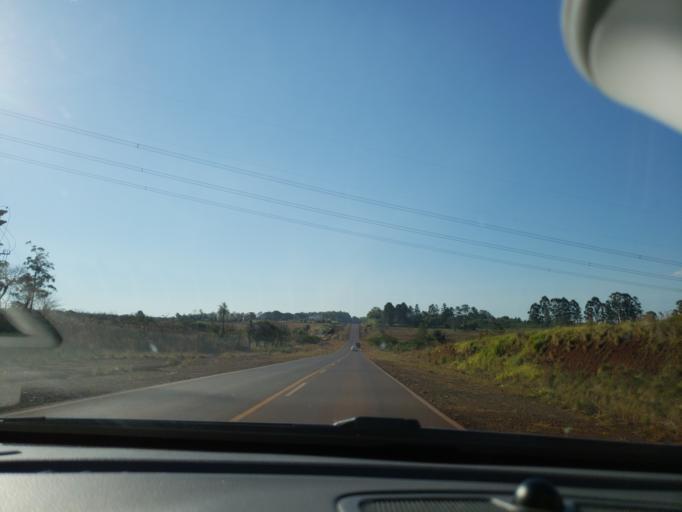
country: AR
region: Misiones
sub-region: Departamento de Capital
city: Posadas
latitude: -27.4626
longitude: -55.9707
